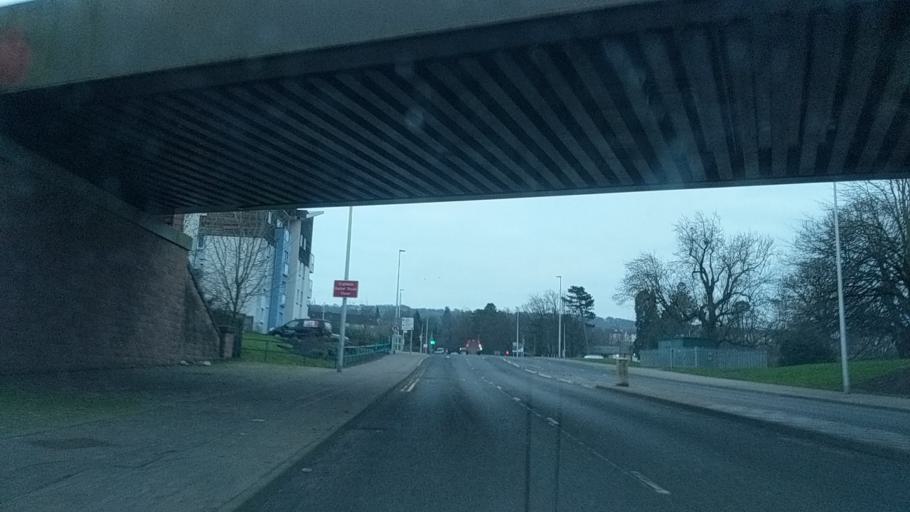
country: GB
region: Scotland
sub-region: South Lanarkshire
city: Rutherglen
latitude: 55.8169
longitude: -4.2149
